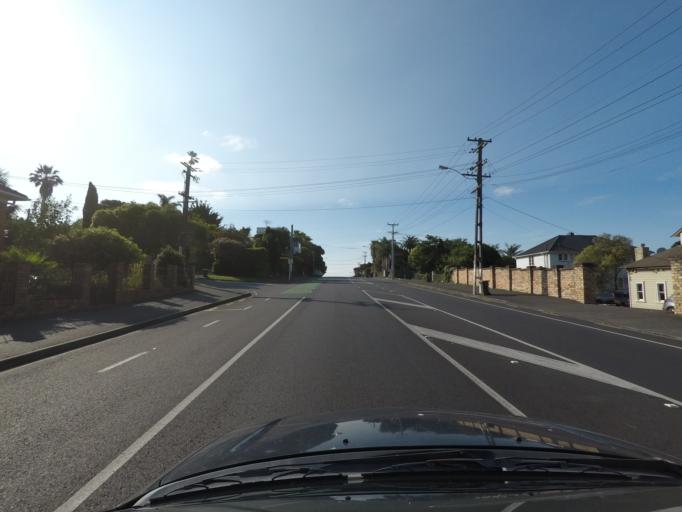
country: NZ
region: Auckland
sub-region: Auckland
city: Auckland
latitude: -36.8872
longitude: 174.7201
